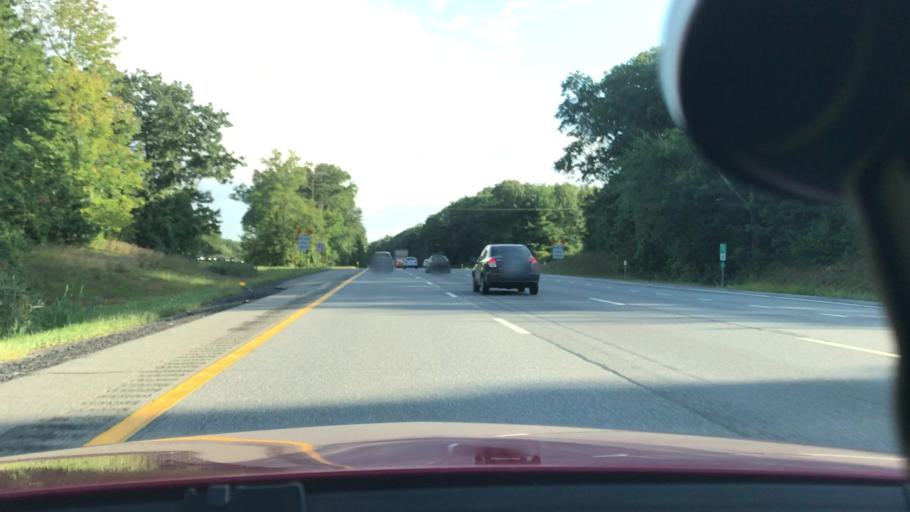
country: US
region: New York
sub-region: Albany County
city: Cohoes
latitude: 42.8152
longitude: -73.7674
